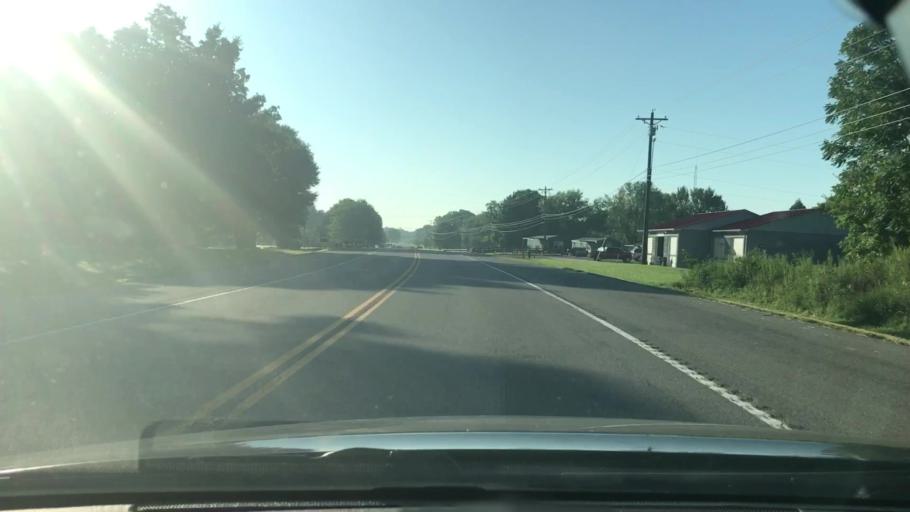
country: US
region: Tennessee
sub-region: Sumner County
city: Millersville
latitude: 36.4131
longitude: -86.7095
